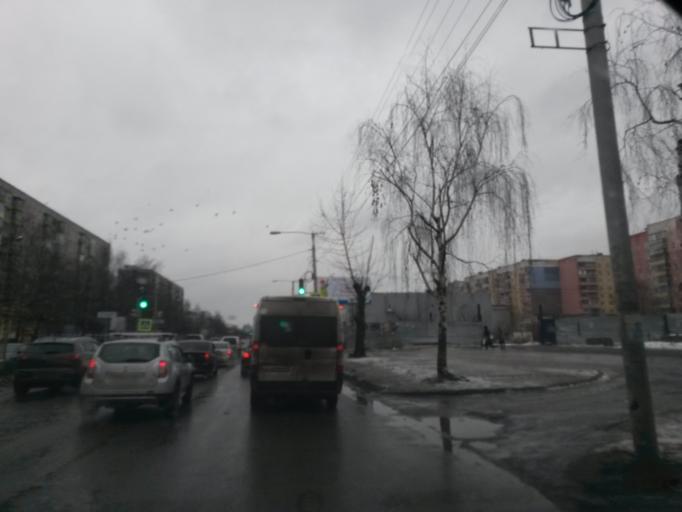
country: RU
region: Jaroslavl
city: Yaroslavl
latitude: 57.6477
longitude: 39.9525
